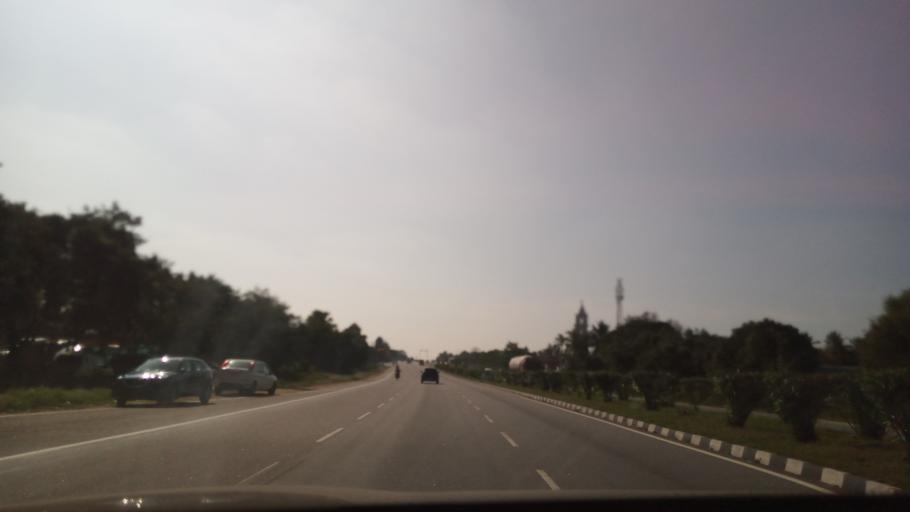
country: IN
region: Tamil Nadu
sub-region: Krishnagiri
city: Krishnagiri
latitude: 12.5361
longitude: 78.2709
